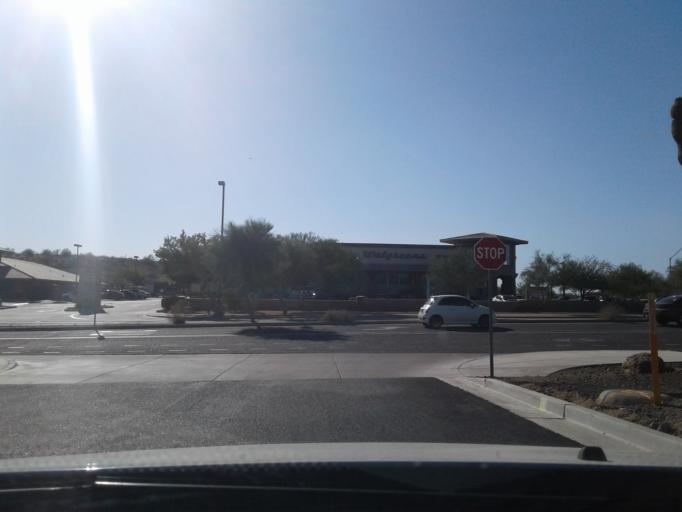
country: US
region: Arizona
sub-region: Maricopa County
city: Anthem
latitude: 33.7976
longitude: -112.1178
